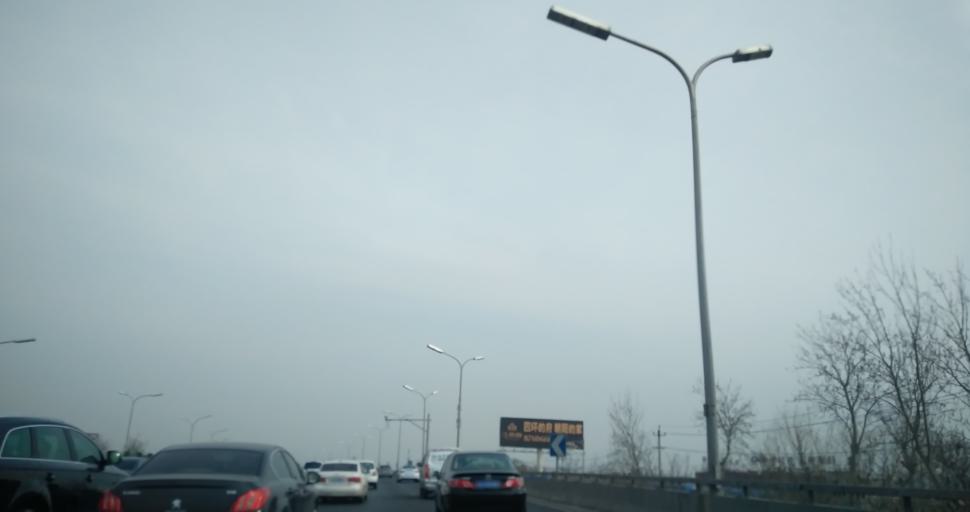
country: CN
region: Beijing
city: Jiugong
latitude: 39.8455
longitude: 116.4779
